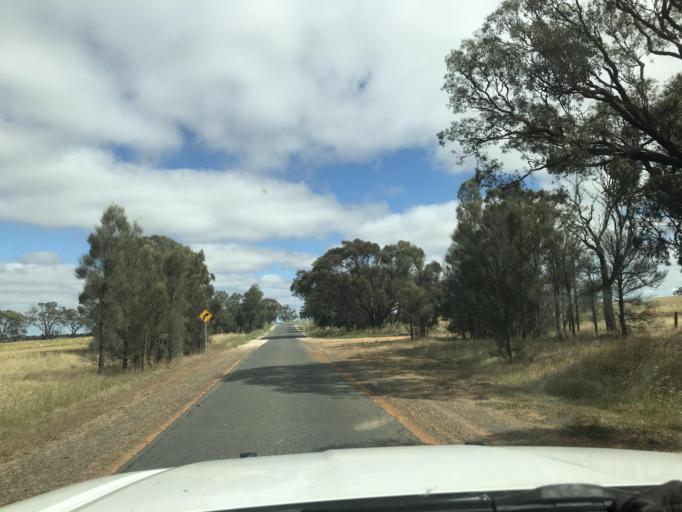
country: AU
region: South Australia
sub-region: Tatiara
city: Bordertown
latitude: -36.3421
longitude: 141.0893
